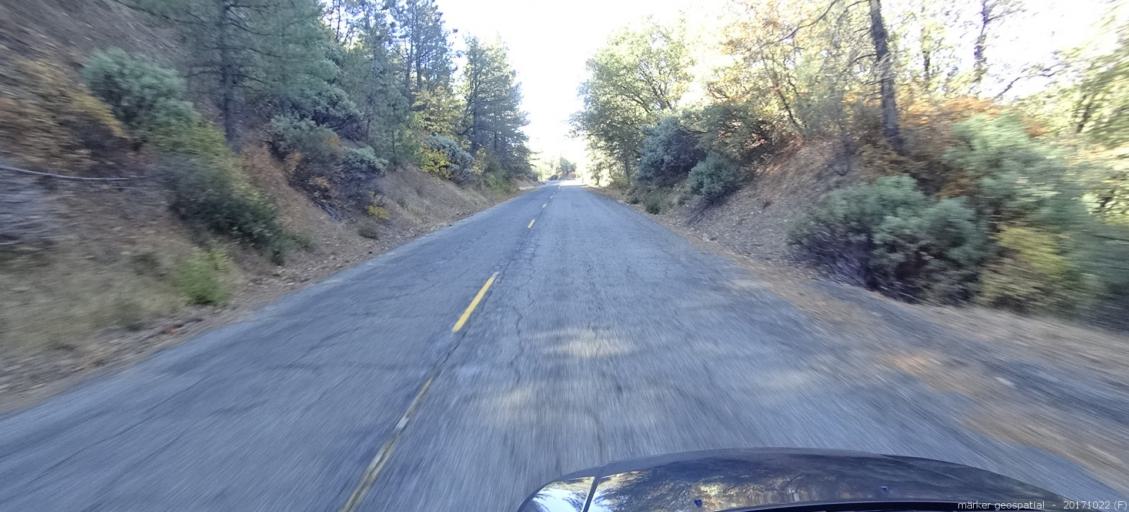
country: US
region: California
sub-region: Shasta County
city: Shasta Lake
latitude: 40.8606
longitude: -122.3565
